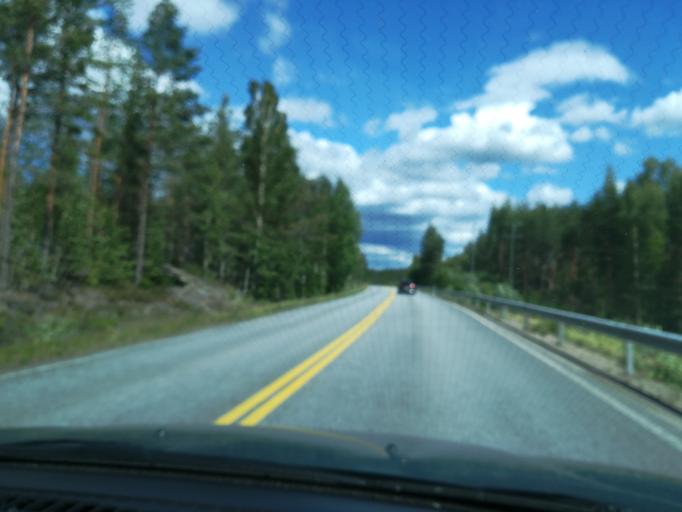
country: FI
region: Southern Savonia
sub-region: Mikkeli
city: Hirvensalmi
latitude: 61.6602
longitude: 26.9498
